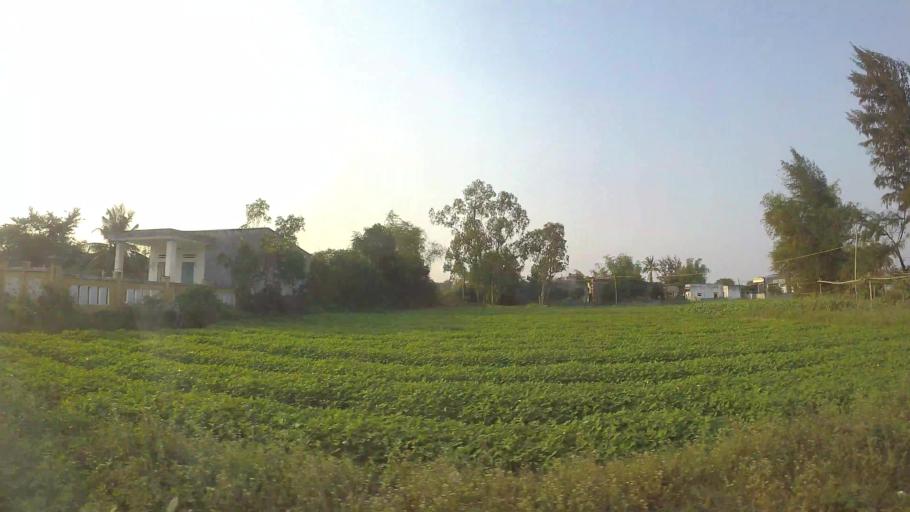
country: VN
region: Da Nang
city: Ngu Hanh Son
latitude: 15.9699
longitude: 108.2464
